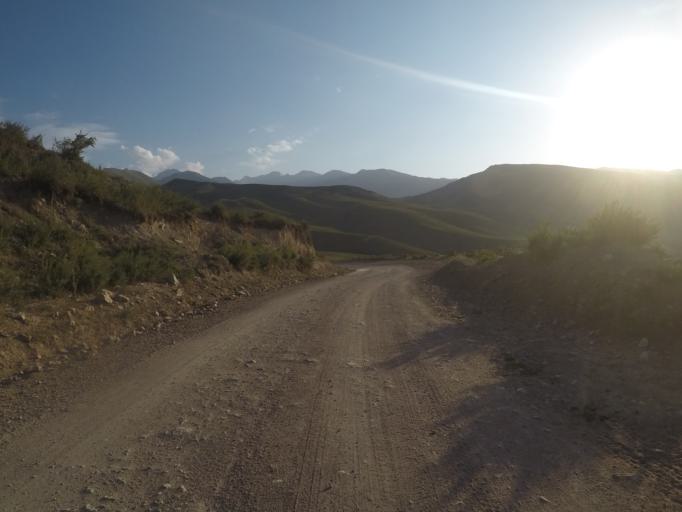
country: KG
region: Chuy
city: Bishkek
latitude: 42.6564
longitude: 74.6614
